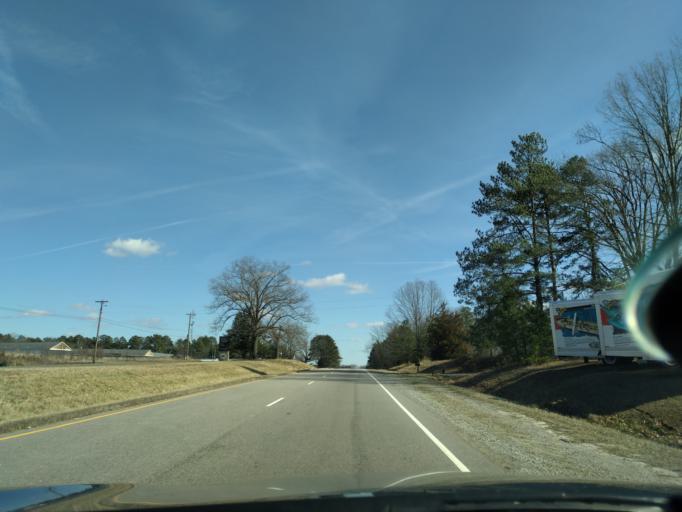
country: US
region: Virginia
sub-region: Nottoway County
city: Crewe
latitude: 37.1900
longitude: -78.1624
